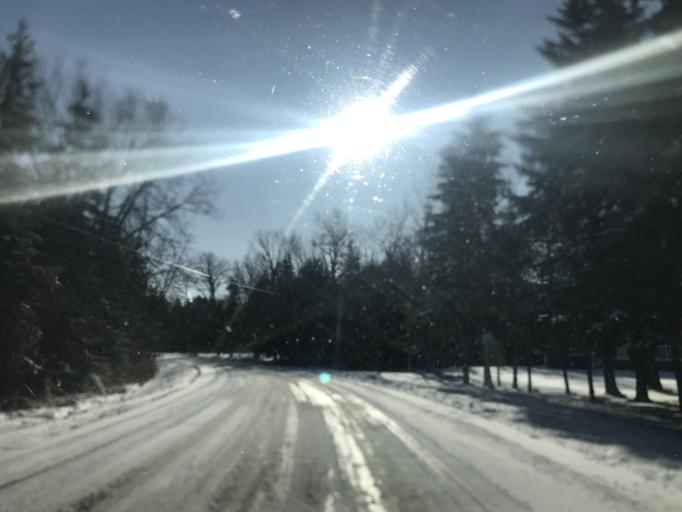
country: US
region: Wisconsin
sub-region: Door County
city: Sturgeon Bay
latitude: 44.8478
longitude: -87.5104
